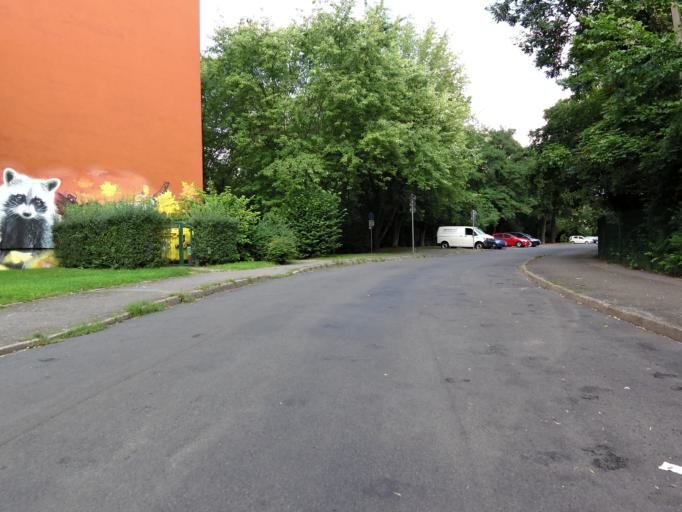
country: DE
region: Saxony
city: Leipzig
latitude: 51.3768
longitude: 12.4191
